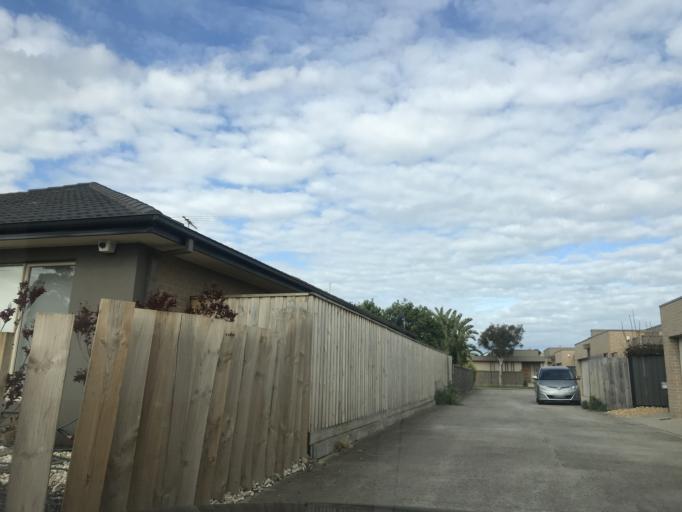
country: AU
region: Victoria
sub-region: Wyndham
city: Williams Landing
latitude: -37.8874
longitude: 144.7355
